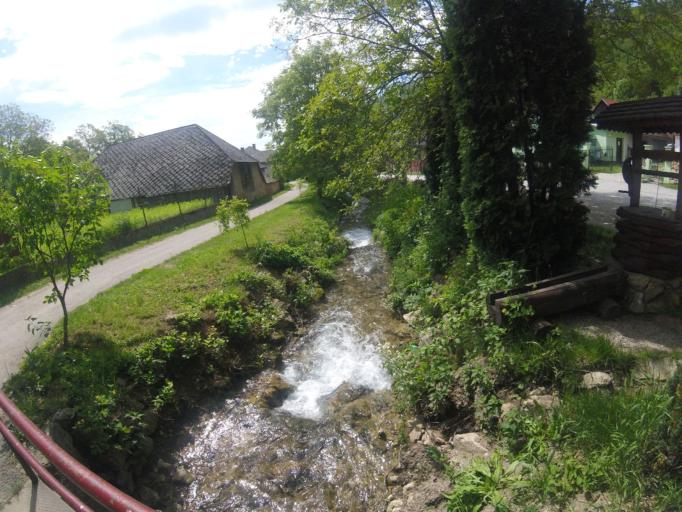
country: SK
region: Kosicky
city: Medzev
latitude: 48.6317
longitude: 20.8505
